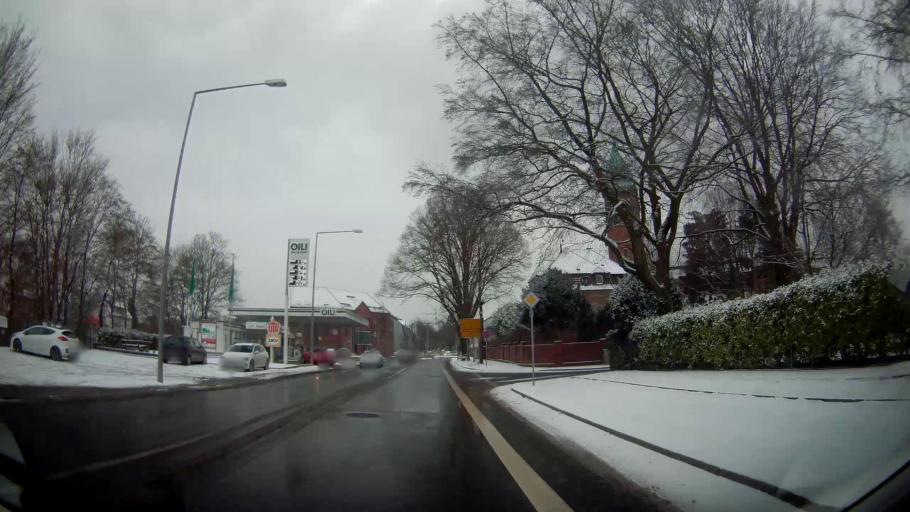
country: DE
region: North Rhine-Westphalia
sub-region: Regierungsbezirk Munster
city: Gladbeck
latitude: 51.5899
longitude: 6.9850
